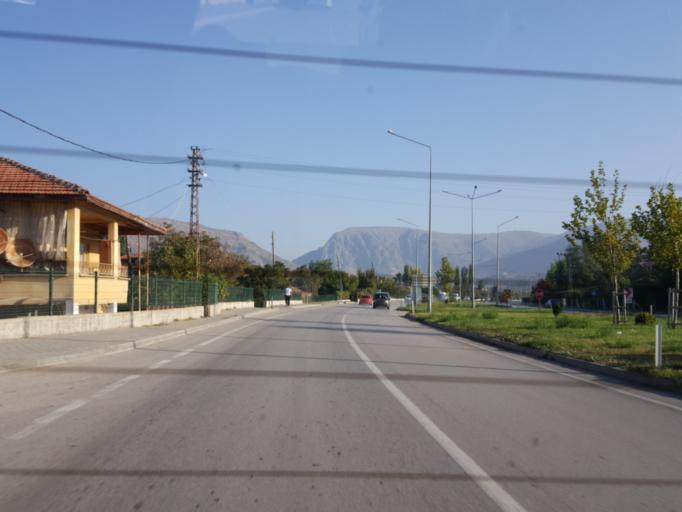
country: TR
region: Amasya
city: Amasya
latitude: 40.5937
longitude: 35.8025
